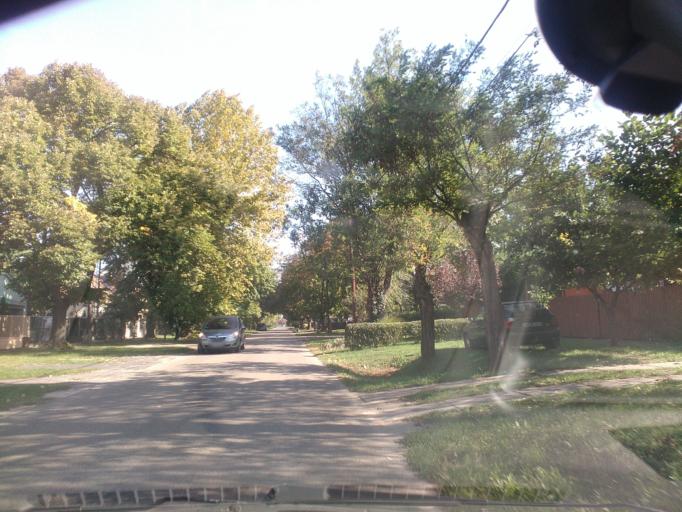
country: HU
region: Pest
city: Gyal
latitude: 47.4242
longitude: 19.2176
